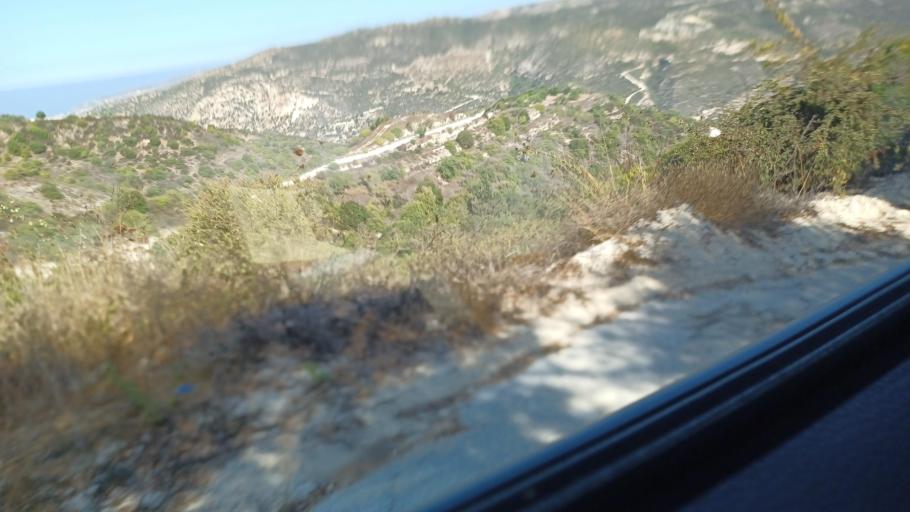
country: CY
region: Pafos
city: Tala
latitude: 34.8637
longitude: 32.4510
